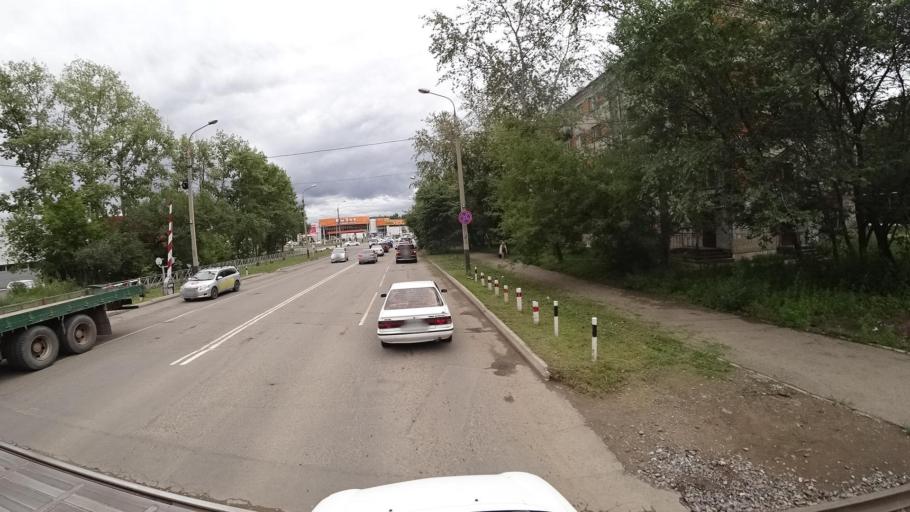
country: RU
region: Khabarovsk Krai
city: Komsomolsk-on-Amur
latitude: 50.5597
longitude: 137.0225
